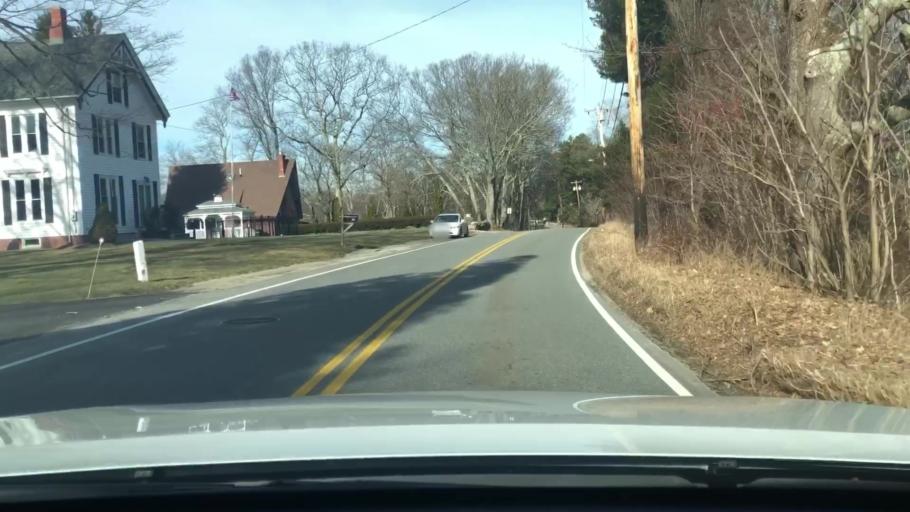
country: US
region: Massachusetts
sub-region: Worcester County
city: Blackstone
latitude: 42.0472
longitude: -71.5201
